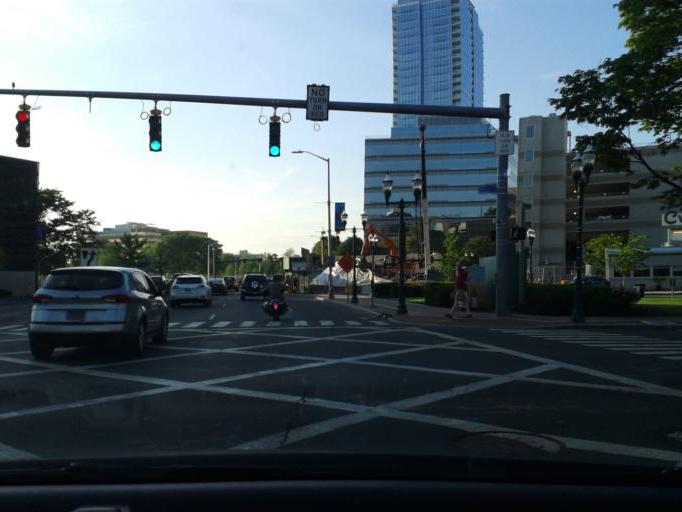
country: US
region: Connecticut
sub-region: Fairfield County
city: Stamford
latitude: 41.0526
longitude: -73.5425
